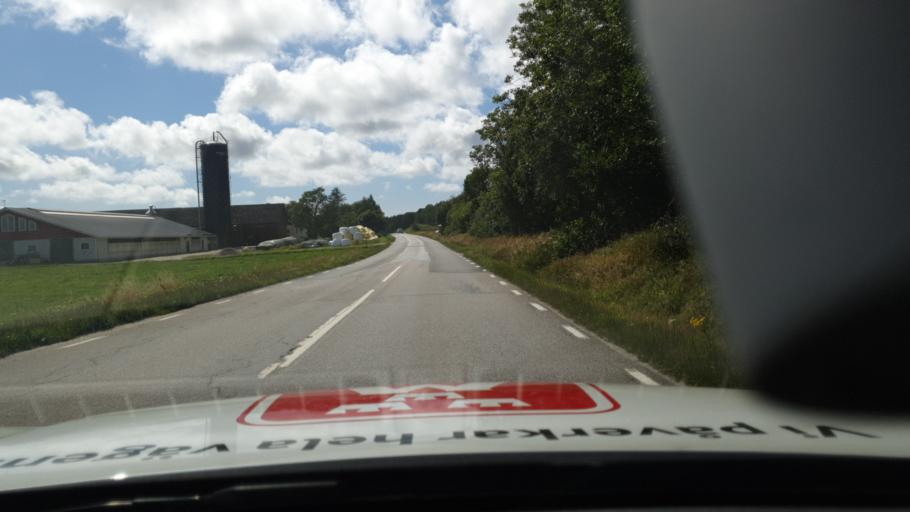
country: SE
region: Vaestra Goetaland
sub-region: Orust
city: Henan
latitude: 58.1466
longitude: 11.5799
